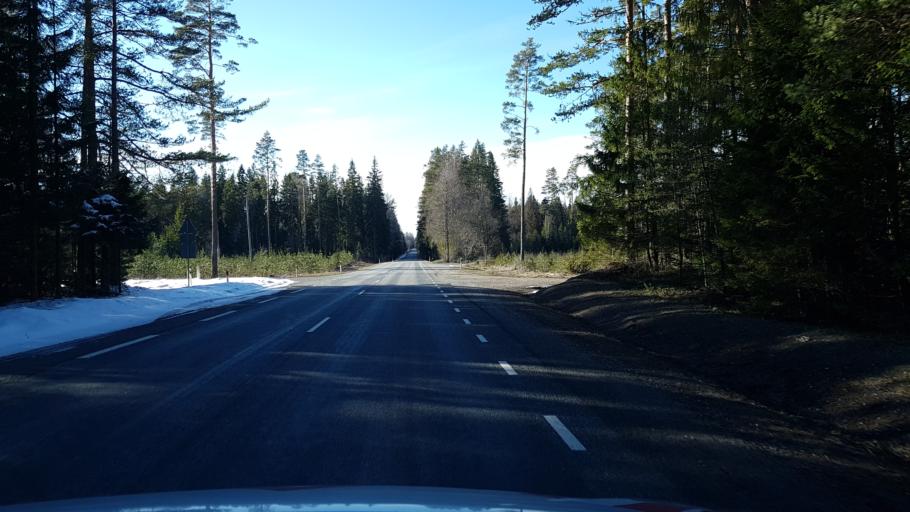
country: EE
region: Laeaene-Virumaa
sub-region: Tapa vald
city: Tapa
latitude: 59.4283
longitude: 25.9775
